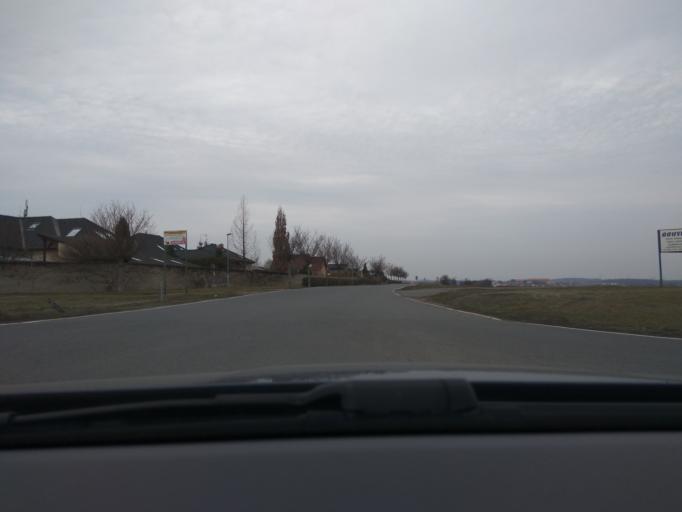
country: CZ
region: Central Bohemia
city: Hovorcovice
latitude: 50.1830
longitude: 14.5161
